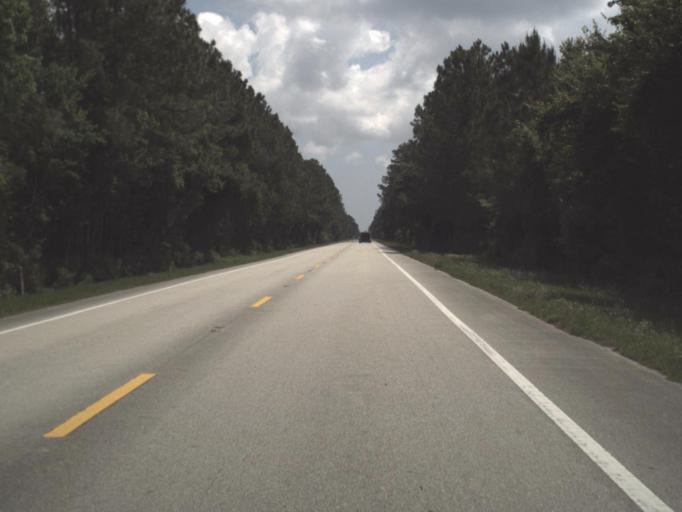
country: US
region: Florida
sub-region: Saint Johns County
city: Saint Augustine Shores
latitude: 29.7303
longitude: -81.3894
